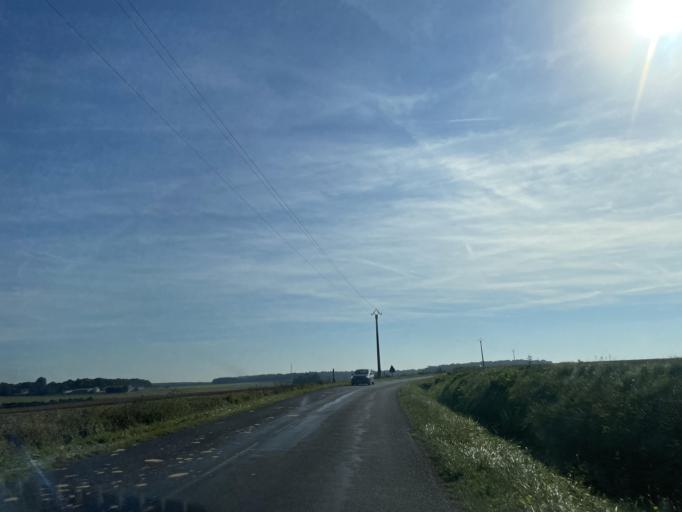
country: FR
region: Ile-de-France
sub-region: Departement de Seine-et-Marne
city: Saint-Jean-les-Deux-Jumeaux
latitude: 48.9318
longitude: 2.9943
